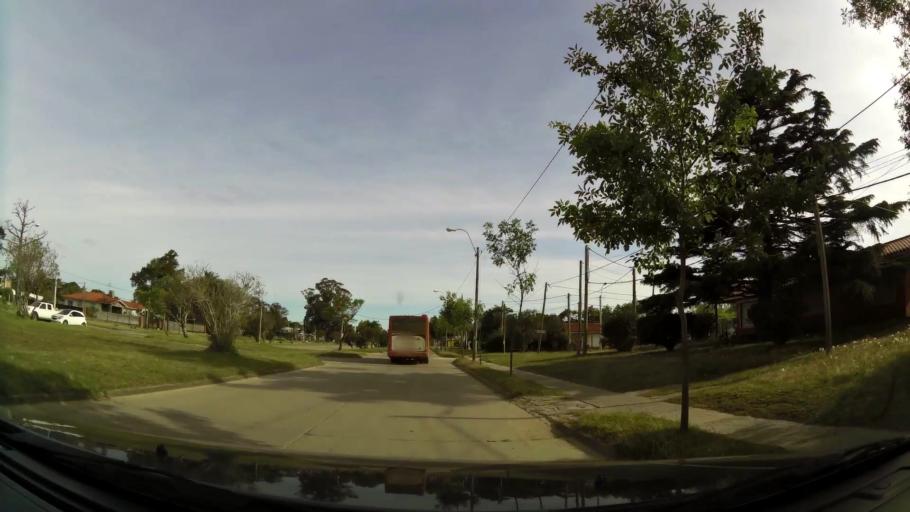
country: UY
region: Canelones
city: Atlantida
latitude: -34.7786
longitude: -55.8395
